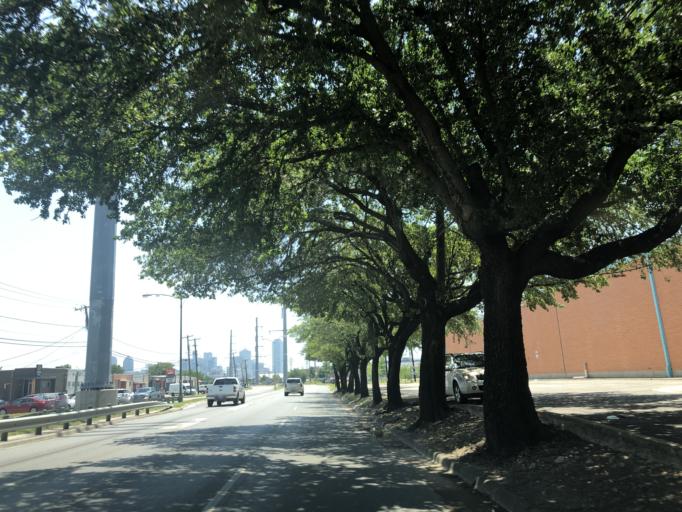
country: US
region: Texas
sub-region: Dallas County
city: Dallas
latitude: 32.7980
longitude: -96.8391
